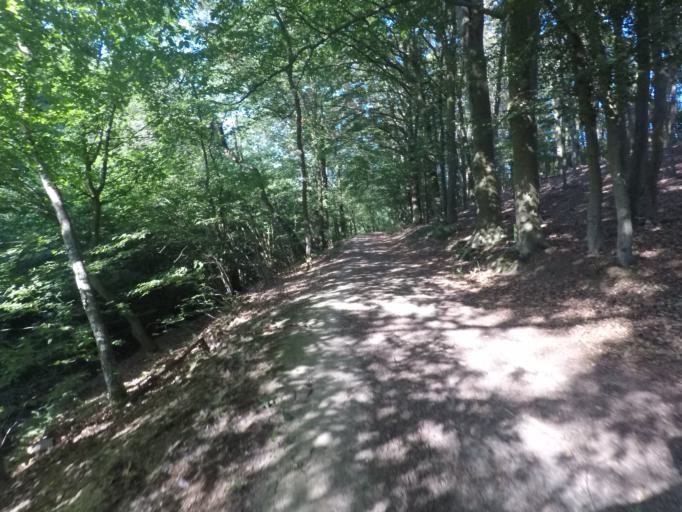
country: DE
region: North Rhine-Westphalia
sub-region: Regierungsbezirk Detmold
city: Hiddenhausen
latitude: 52.1204
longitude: 8.6233
